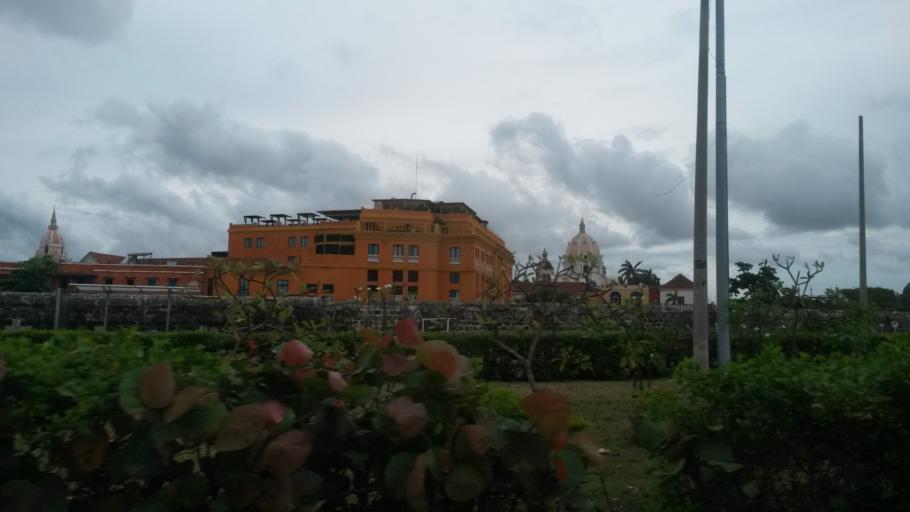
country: CO
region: Bolivar
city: Cartagena
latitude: 10.4222
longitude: -75.5537
